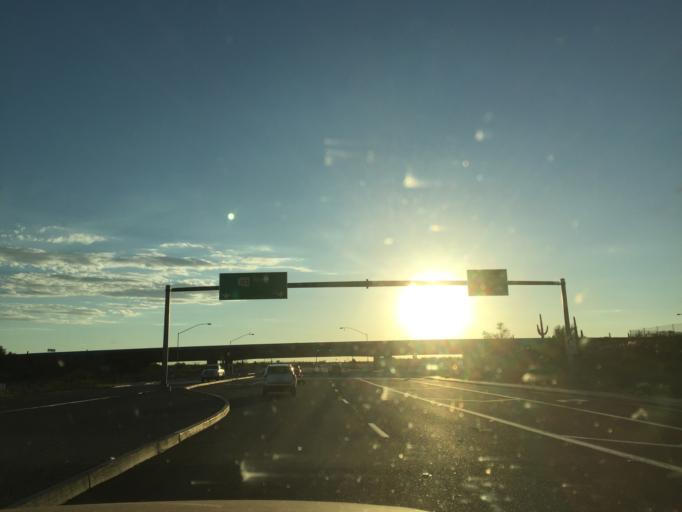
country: US
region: Arizona
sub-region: Maricopa County
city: Sun City West
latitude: 33.7137
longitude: -112.3086
